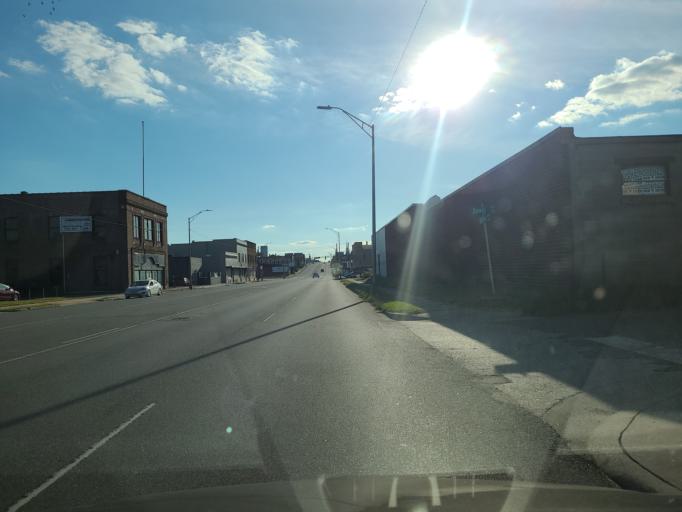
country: US
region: North Carolina
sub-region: Gaston County
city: Gastonia
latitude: 35.2624
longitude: -81.1718
